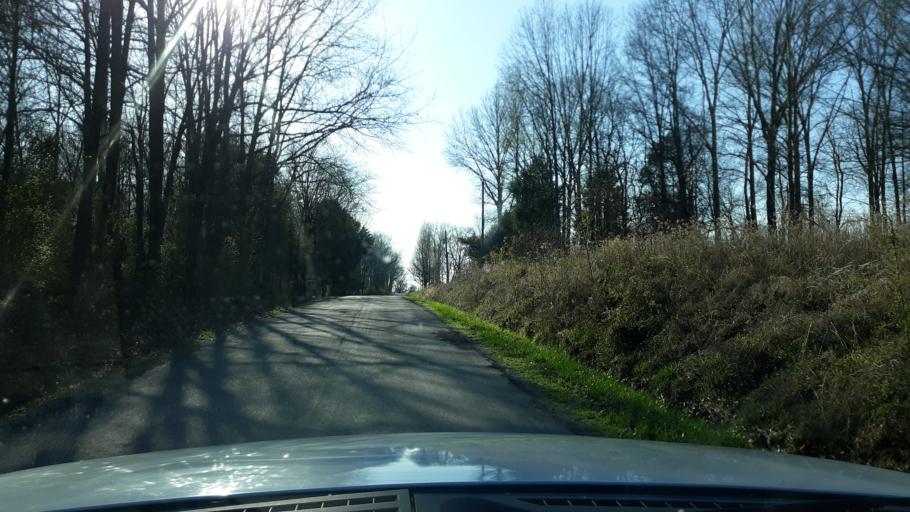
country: US
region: Illinois
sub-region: Saline County
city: Harrisburg
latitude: 37.7627
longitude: -88.5764
